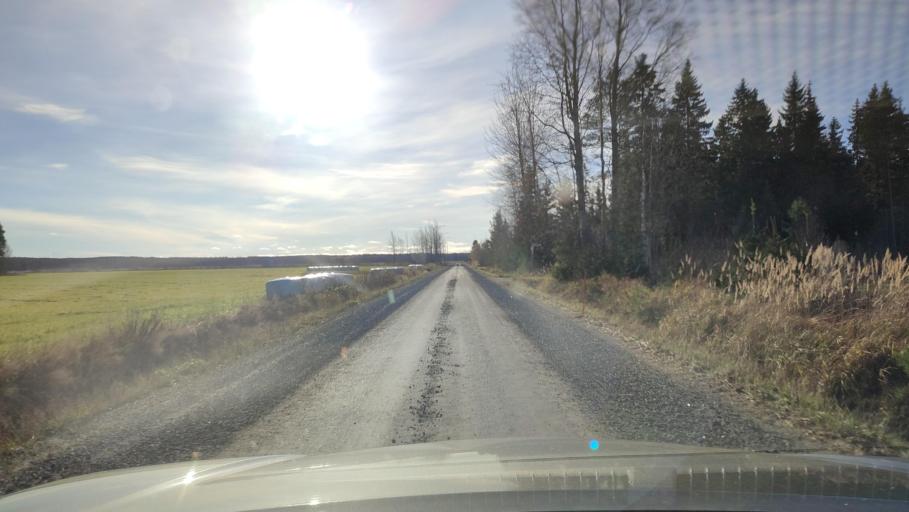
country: FI
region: Southern Ostrobothnia
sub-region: Suupohja
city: Teuva
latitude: 62.4494
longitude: 21.6133
